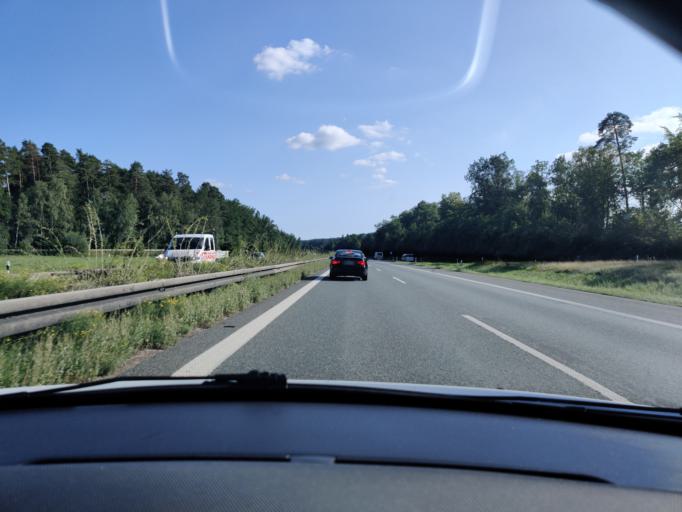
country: DE
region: Bavaria
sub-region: Upper Palatinate
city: Wackersdorf
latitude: 49.3425
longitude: 12.1498
